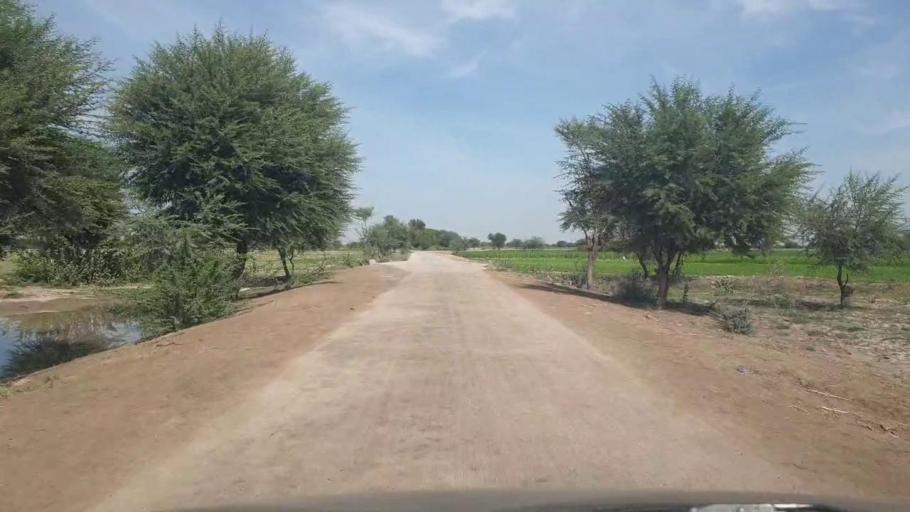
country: PK
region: Sindh
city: Kunri
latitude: 25.2138
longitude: 69.6318
